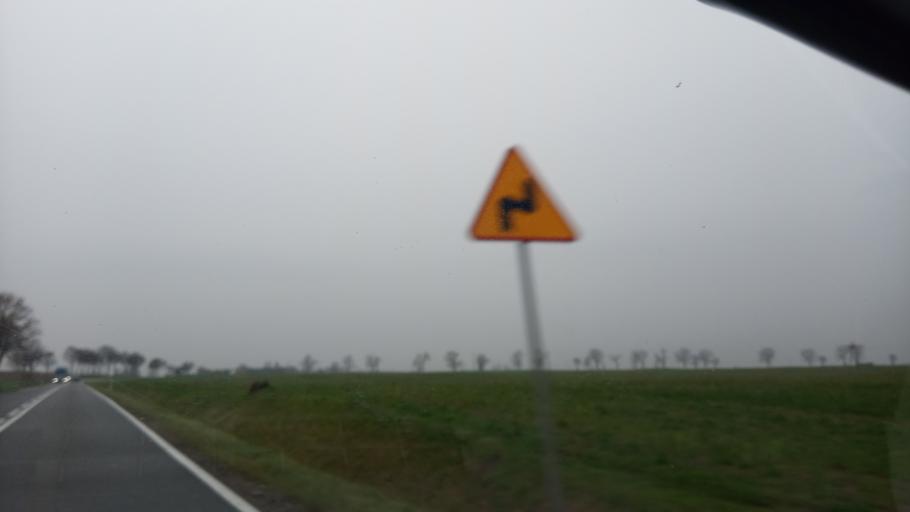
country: PL
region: Kujawsko-Pomorskie
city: Kamien Krajenski
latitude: 53.5107
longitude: 17.5101
